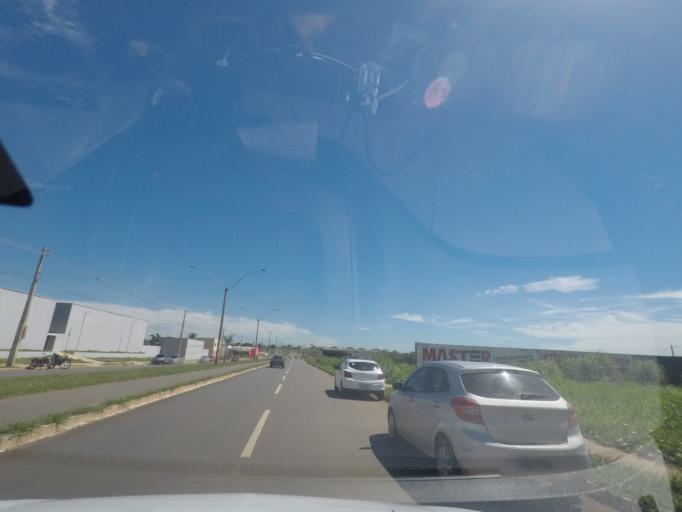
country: BR
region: Goias
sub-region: Aparecida De Goiania
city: Aparecida de Goiania
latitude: -16.7990
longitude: -49.3287
